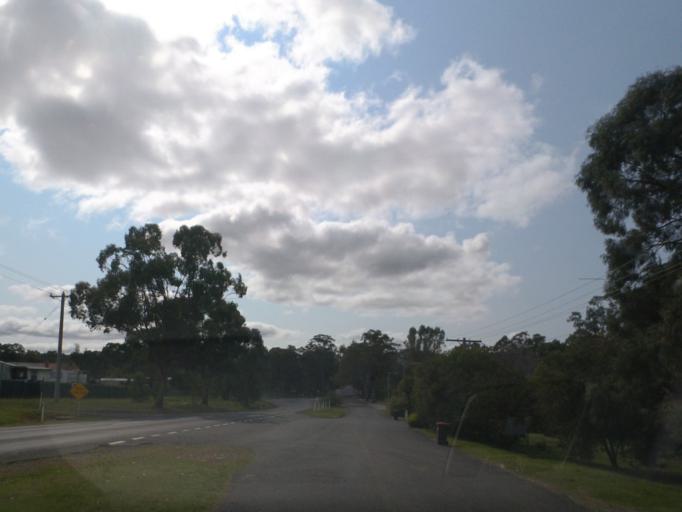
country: AU
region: Victoria
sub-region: Murrindindi
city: Kinglake West
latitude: -37.0930
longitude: 145.1040
